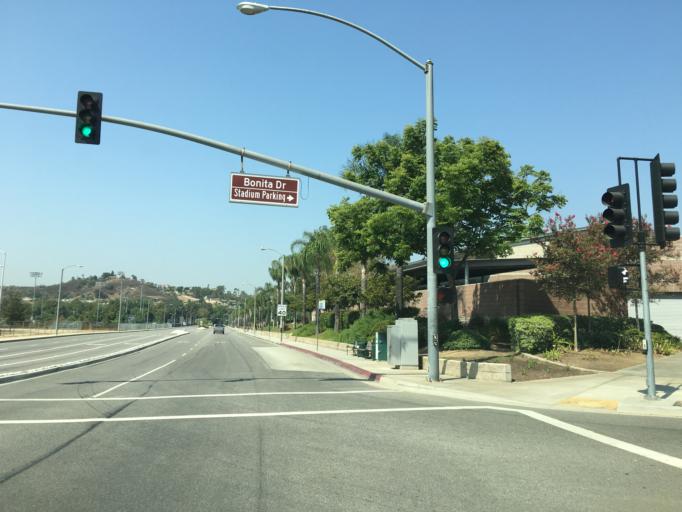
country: US
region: California
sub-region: Los Angeles County
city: Diamond Bar
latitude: 34.0469
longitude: -117.8403
